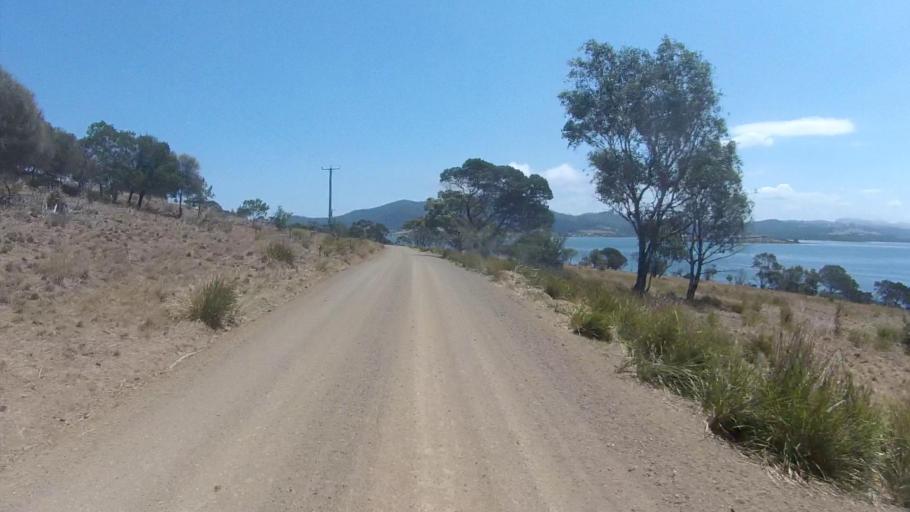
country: AU
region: Tasmania
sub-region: Sorell
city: Sorell
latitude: -42.8924
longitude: 147.8556
